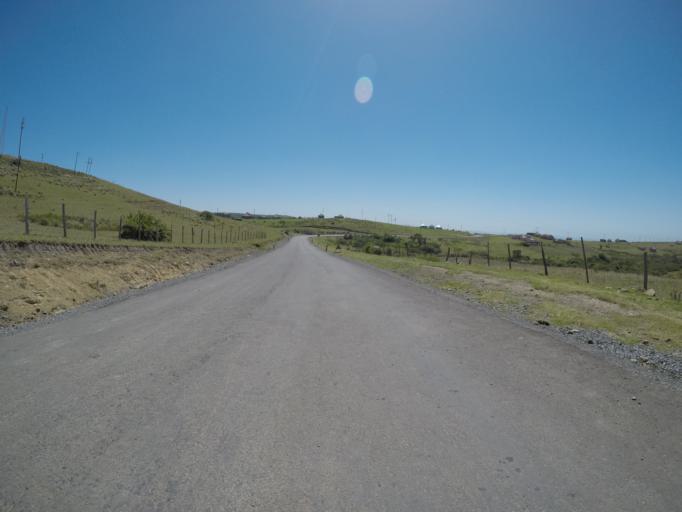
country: ZA
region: Eastern Cape
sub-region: OR Tambo District Municipality
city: Libode
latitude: -32.0002
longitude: 29.1197
